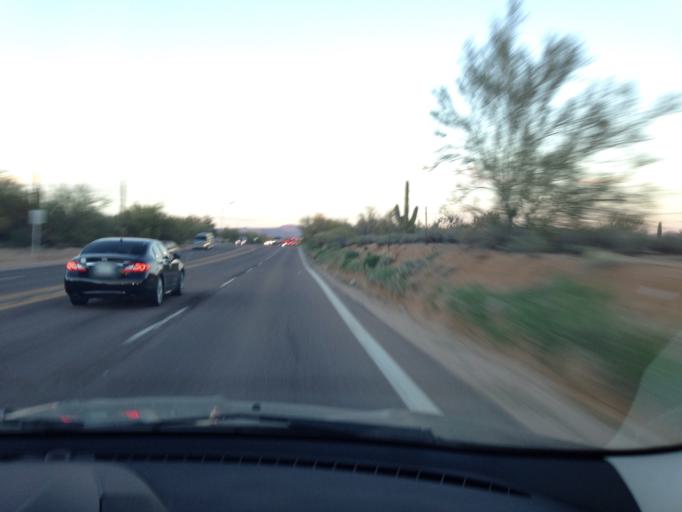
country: US
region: Arizona
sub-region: Maricopa County
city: Cave Creek
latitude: 33.7358
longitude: -111.9781
